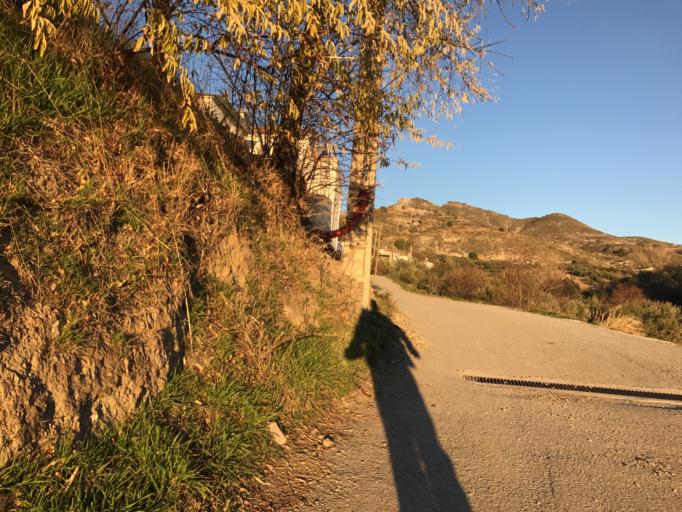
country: ES
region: Andalusia
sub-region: Provincia de Granada
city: Beas de Granada
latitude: 37.2217
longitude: -3.4755
